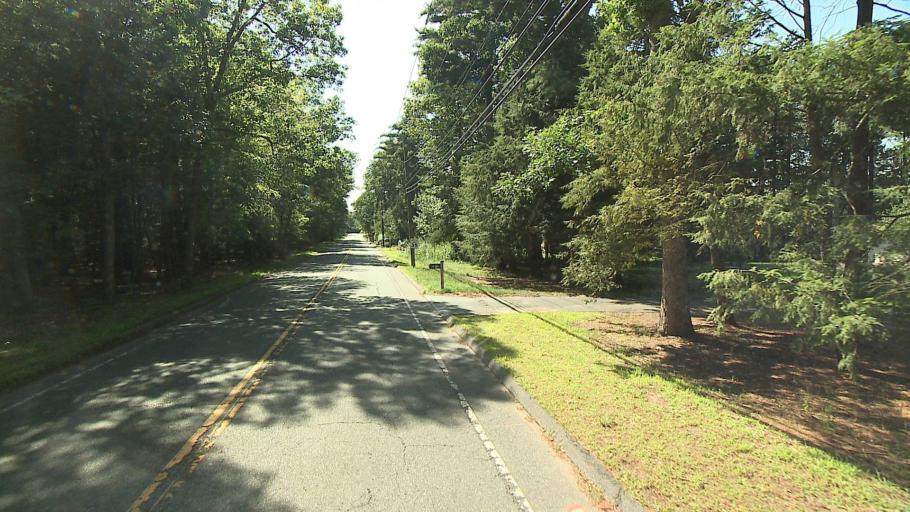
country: US
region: Connecticut
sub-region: Hartford County
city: Simsbury Center
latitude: 41.8692
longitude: -72.8306
